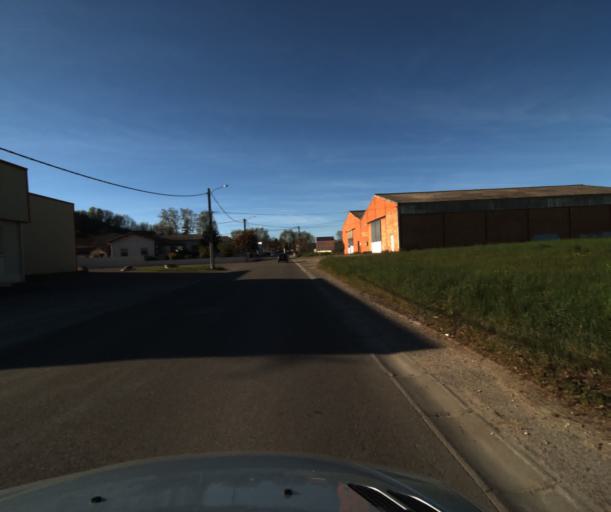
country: FR
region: Midi-Pyrenees
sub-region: Departement du Tarn-et-Garonne
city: Moissac
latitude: 44.1098
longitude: 1.1071
